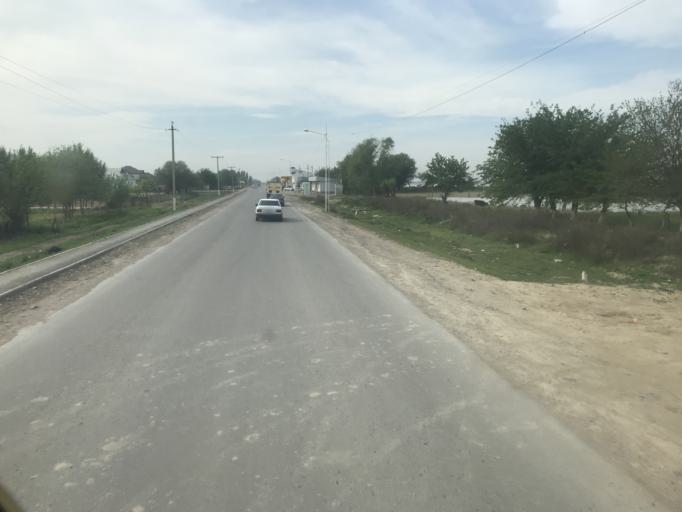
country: KZ
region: Ongtustik Qazaqstan
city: Asykata
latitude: 41.0046
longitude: 68.2145
